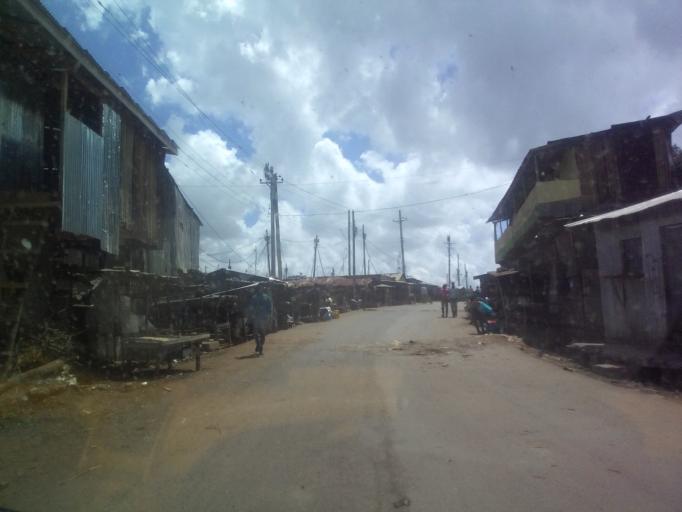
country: KE
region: Nairobi Area
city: Nairobi
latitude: -1.3166
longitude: 36.7766
